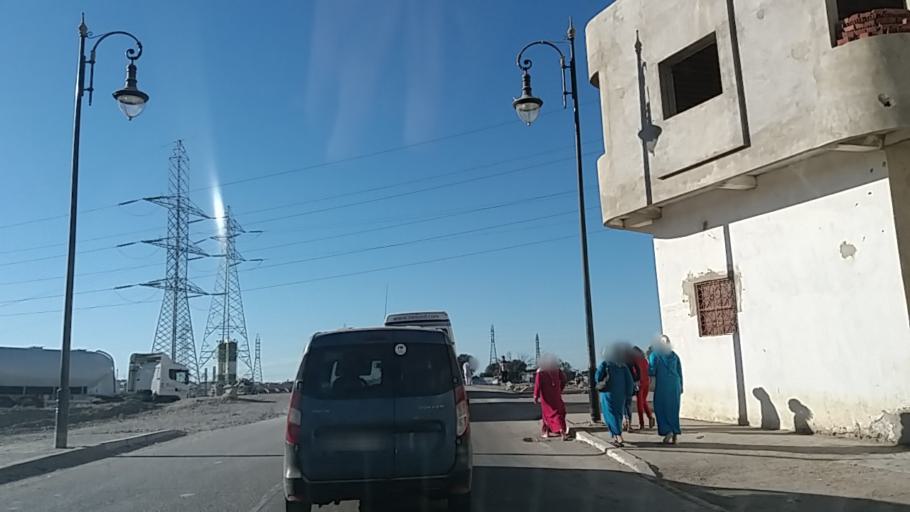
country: MA
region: Tanger-Tetouan
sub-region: Tanger-Assilah
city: Tangier
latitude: 35.7304
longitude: -5.7957
